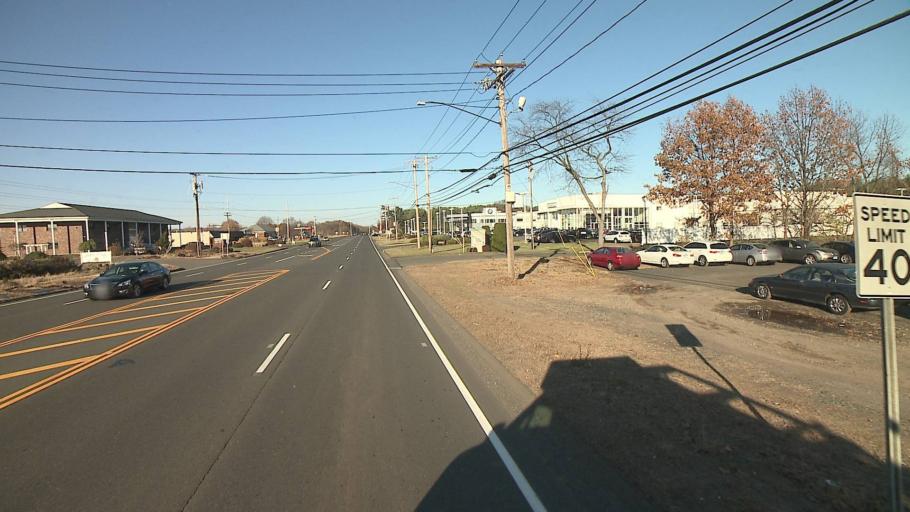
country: US
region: Connecticut
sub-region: New Haven County
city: North Haven
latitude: 41.4200
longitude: -72.8399
